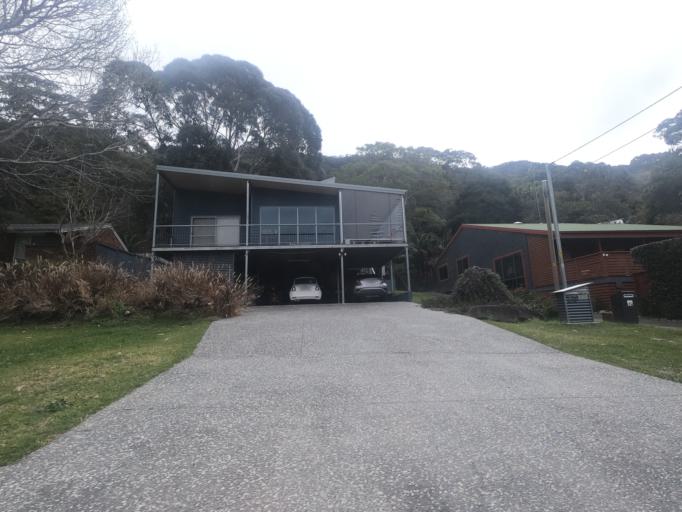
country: AU
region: New South Wales
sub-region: Wollongong
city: Bulli
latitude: -34.2924
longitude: 150.9361
